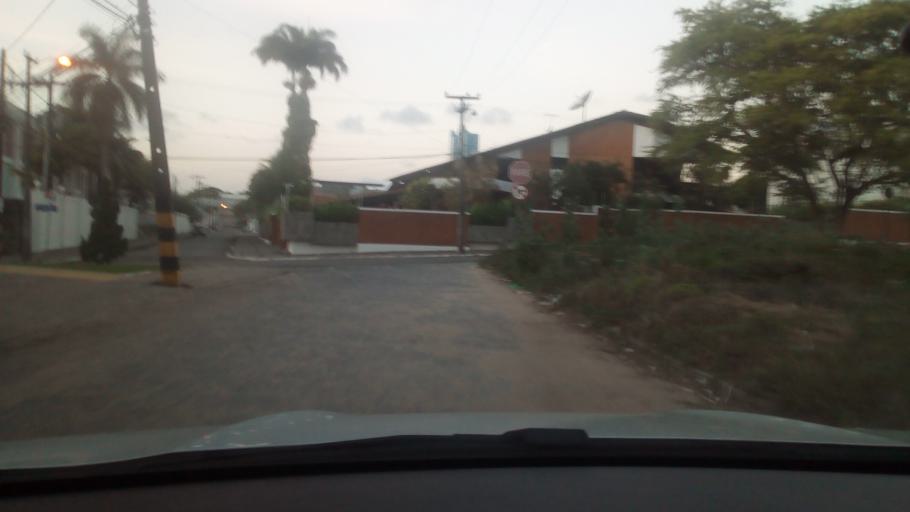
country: BR
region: Paraiba
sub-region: Joao Pessoa
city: Joao Pessoa
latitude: -7.1138
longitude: -34.8432
